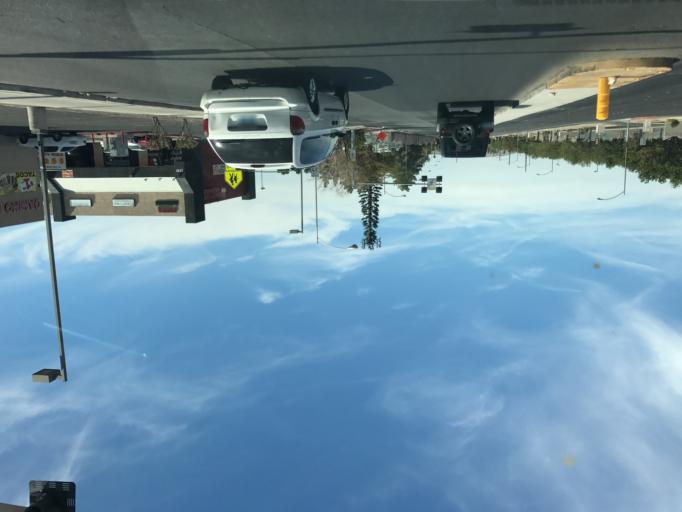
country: US
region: Nevada
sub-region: Clark County
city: Winchester
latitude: 36.1296
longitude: -115.0652
